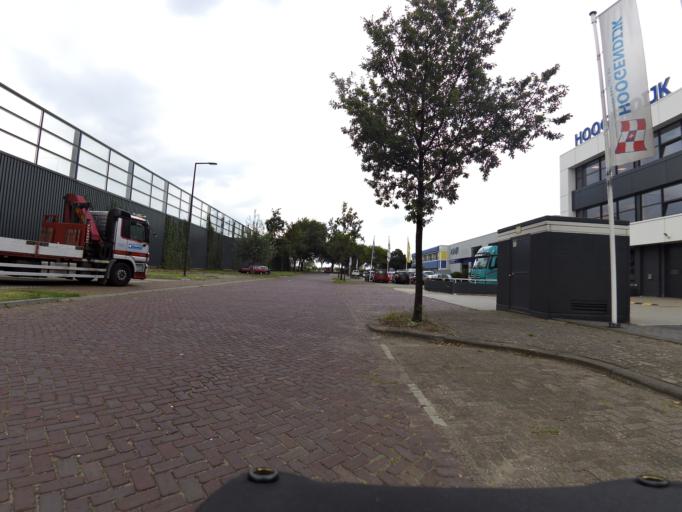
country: NL
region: South Holland
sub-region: Gemeente Vlaardingen
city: Vlaardingen
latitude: 51.8988
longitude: 4.3116
